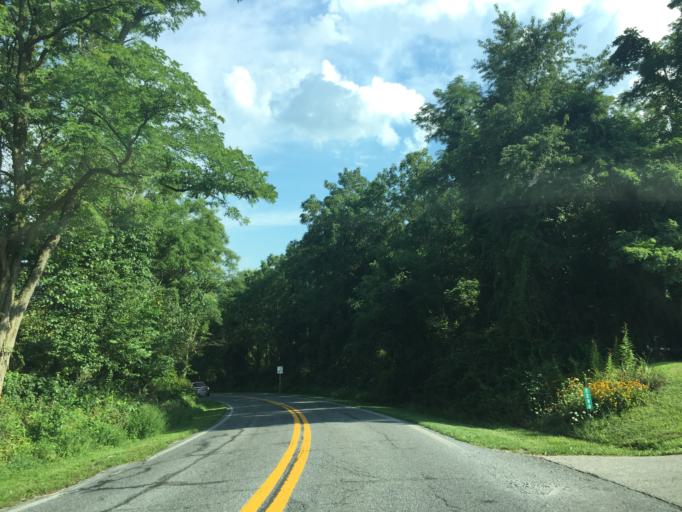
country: US
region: Maryland
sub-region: Carroll County
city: Manchester
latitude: 39.6370
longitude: -76.9068
